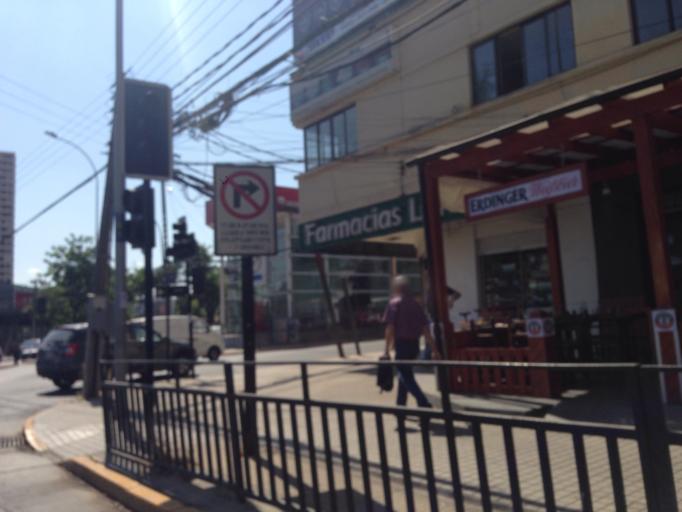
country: CL
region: Santiago Metropolitan
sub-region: Provincia de Santiago
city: Villa Presidente Frei, Nunoa, Santiago, Chile
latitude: -33.4544
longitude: -70.5797
